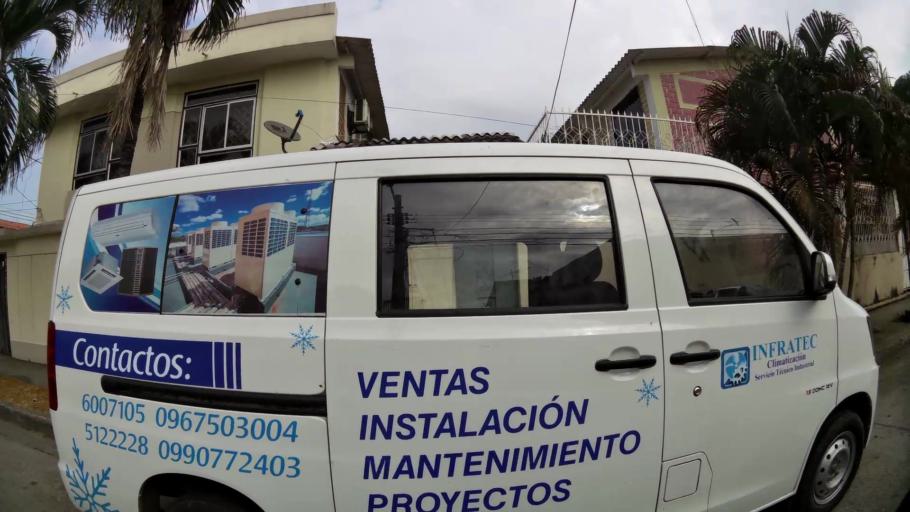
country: EC
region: Guayas
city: Eloy Alfaro
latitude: -2.1397
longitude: -79.8886
